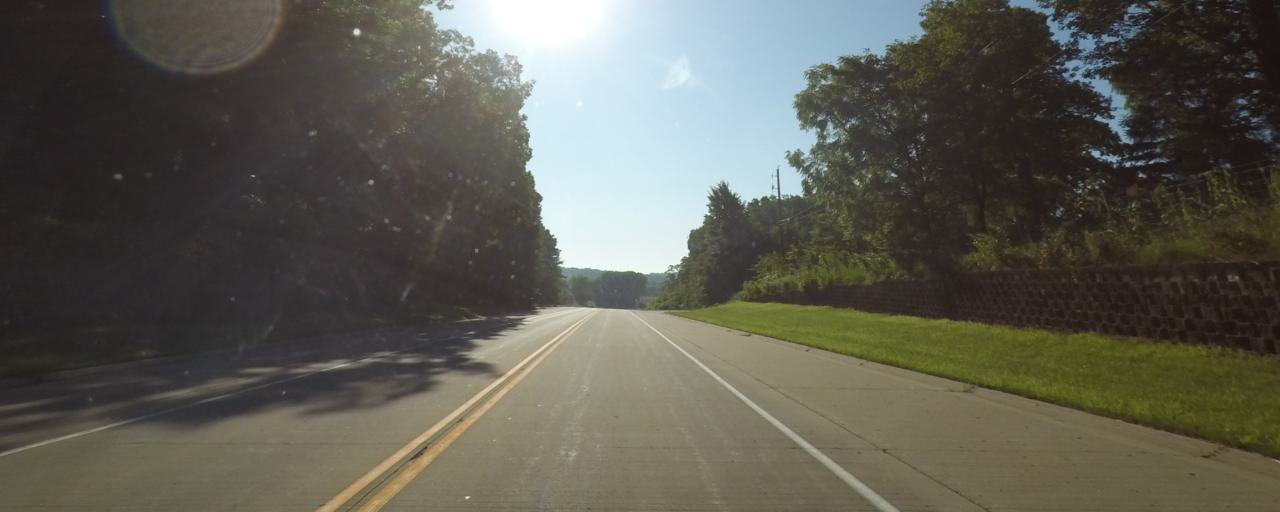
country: US
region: Wisconsin
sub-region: Jefferson County
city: Lake Koshkonong
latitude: 42.9733
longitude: -88.9302
